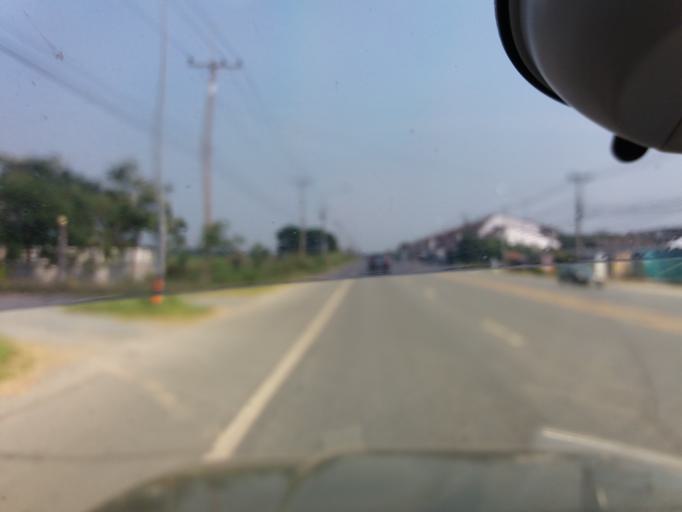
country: TH
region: Sing Buri
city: Bang Racham
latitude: 14.8827
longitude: 100.3319
